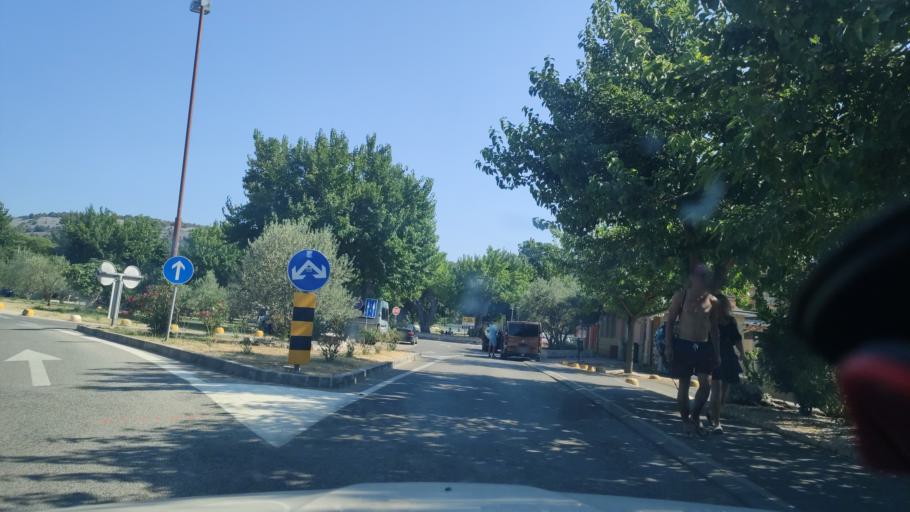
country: HR
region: Sibensko-Kniniska
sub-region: Grad Sibenik
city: Sibenik
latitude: 43.8183
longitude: 15.9242
